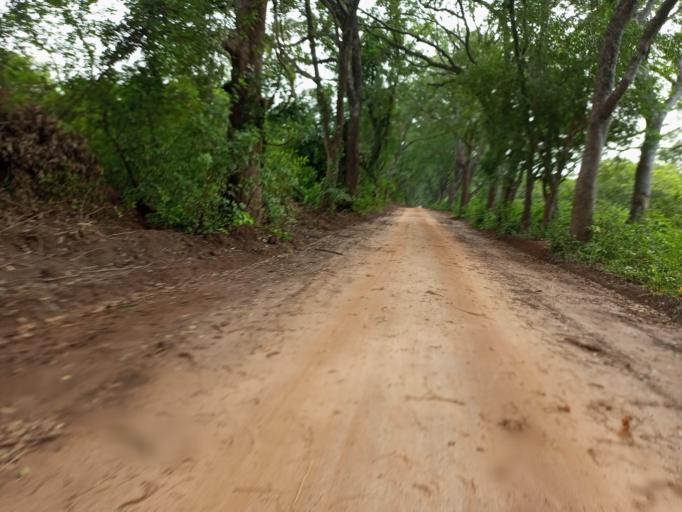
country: GW
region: Oio
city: Bissora
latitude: 12.3930
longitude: -15.6392
